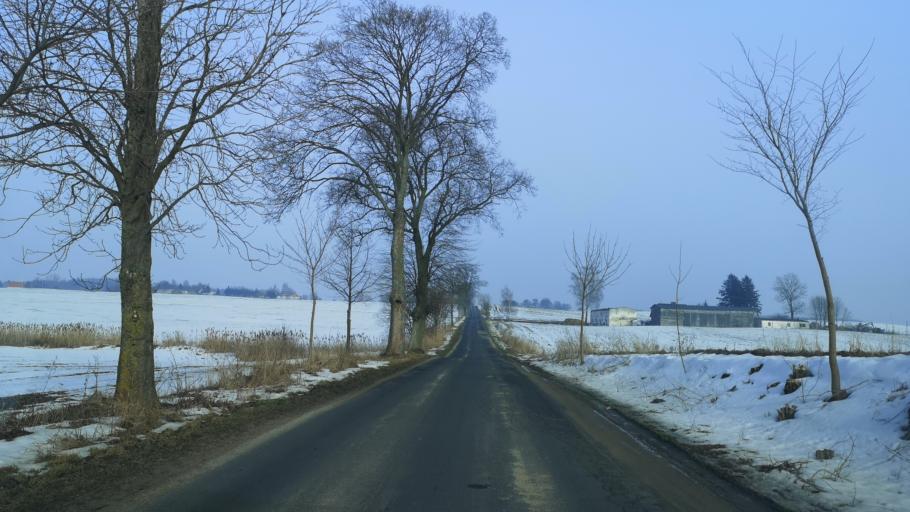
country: PL
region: Warmian-Masurian Voivodeship
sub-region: Powiat nowomiejski
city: Biskupiec
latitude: 53.4924
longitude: 19.3181
